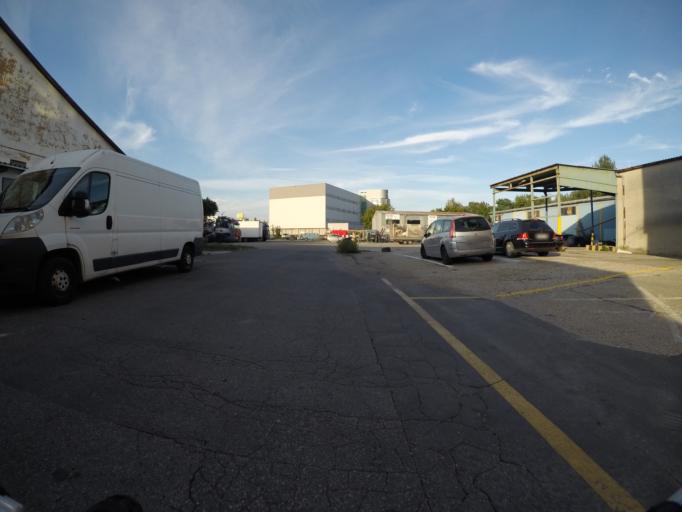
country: SK
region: Bratislavsky
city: Bratislava
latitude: 48.1782
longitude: 17.1702
